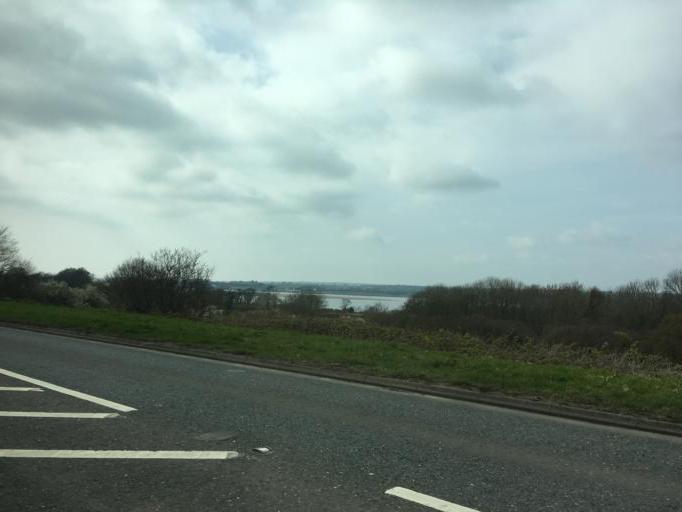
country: GB
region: Wales
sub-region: Gwynedd
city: Caernarfon
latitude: 53.1610
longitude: -4.2496
